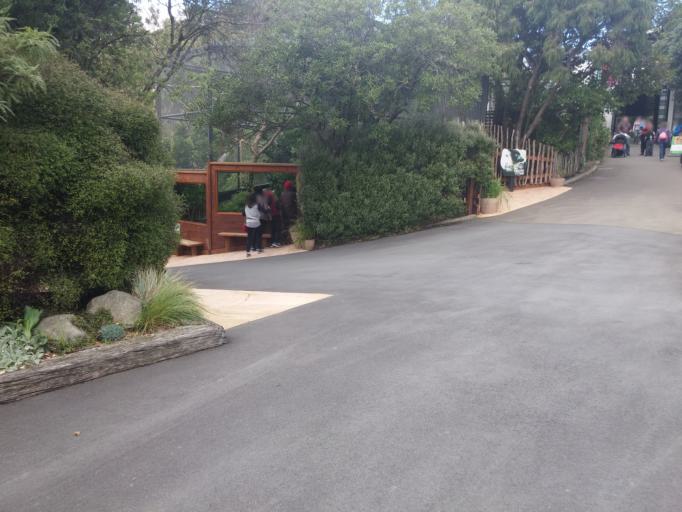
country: NZ
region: Wellington
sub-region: Wellington City
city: Brooklyn
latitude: -41.3208
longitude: 174.7847
